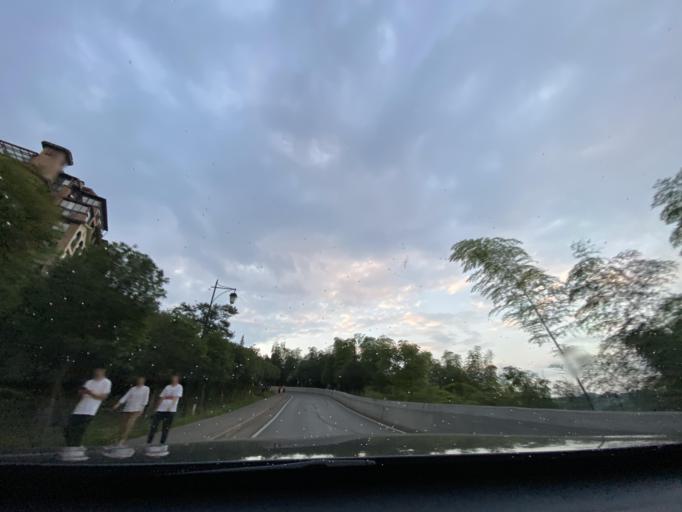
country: CN
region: Guizhou Sheng
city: Changqi
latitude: 28.5405
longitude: 105.9872
